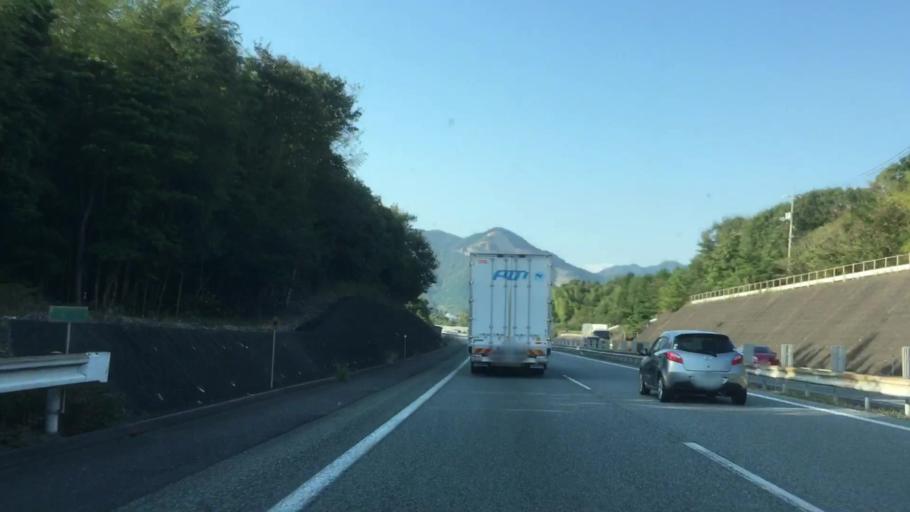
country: JP
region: Yamaguchi
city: Hofu
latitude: 34.0638
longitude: 131.5016
